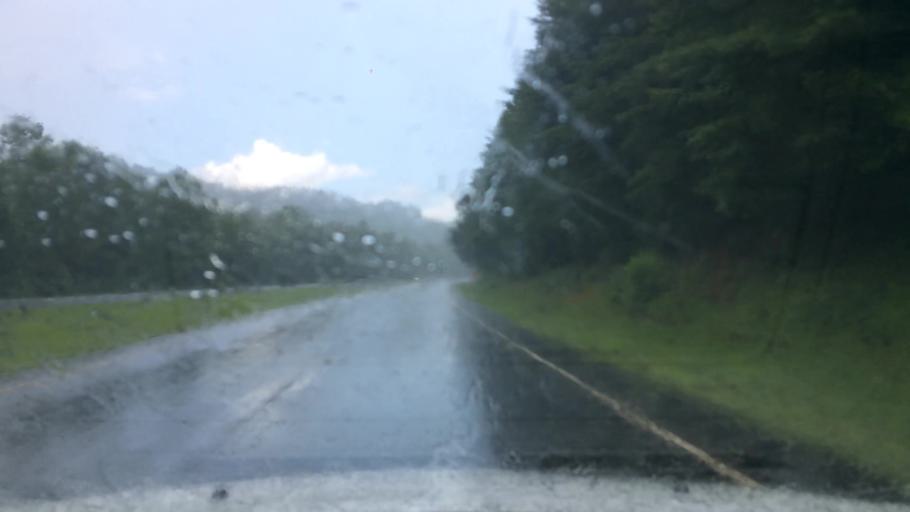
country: US
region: North Carolina
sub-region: Wilkes County
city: Millers Creek
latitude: 36.1952
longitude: -81.4239
